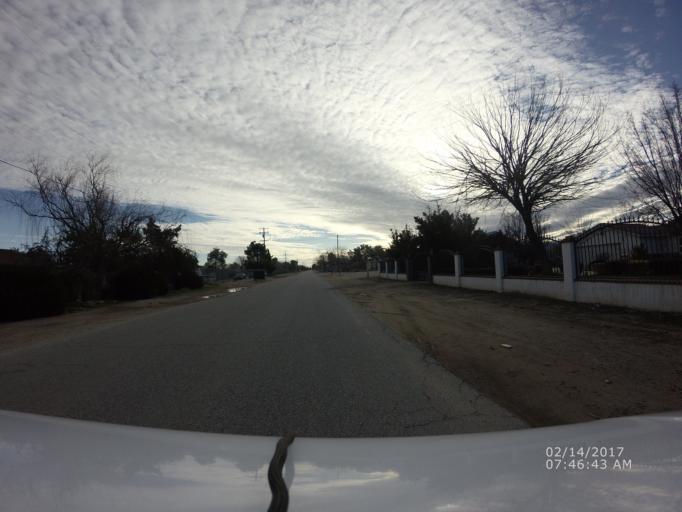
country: US
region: California
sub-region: Los Angeles County
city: Littlerock
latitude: 34.5502
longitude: -117.9554
